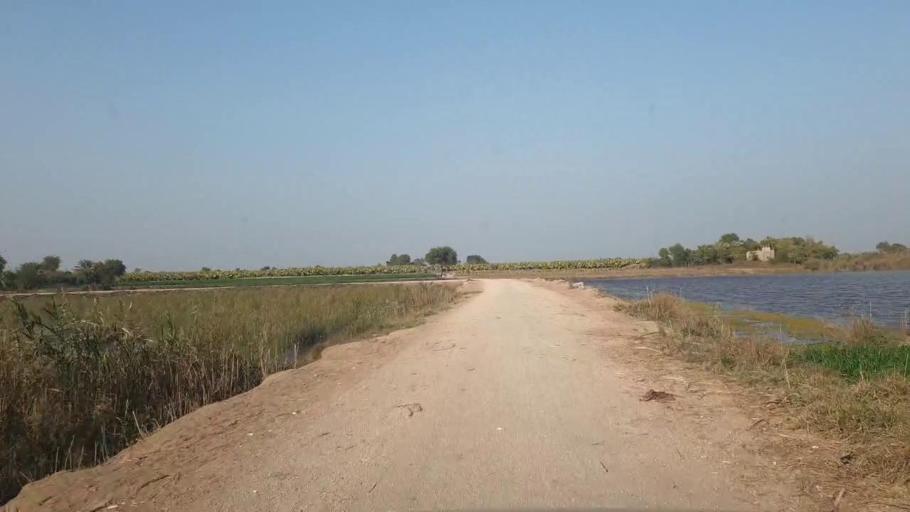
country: PK
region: Sindh
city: Bhit Shah
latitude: 25.8326
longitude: 68.5209
